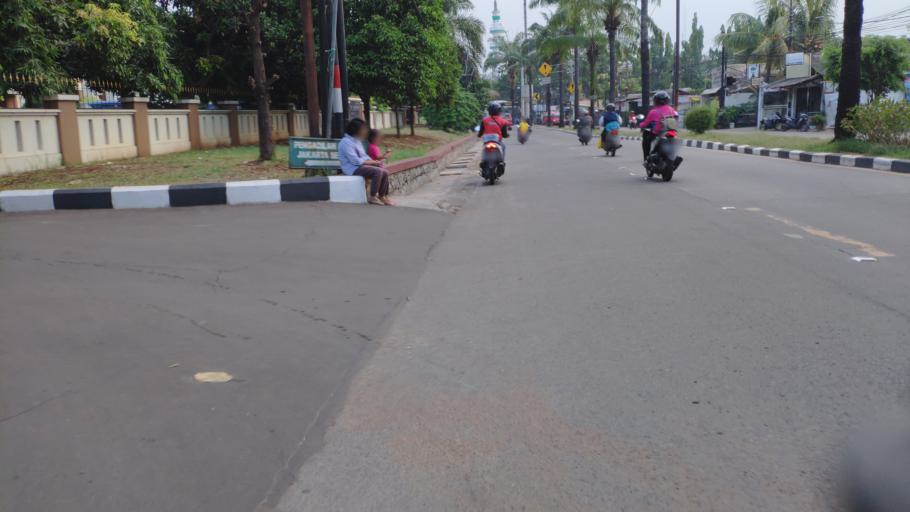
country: ID
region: Jakarta Raya
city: Jakarta
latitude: -6.2993
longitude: 106.8212
